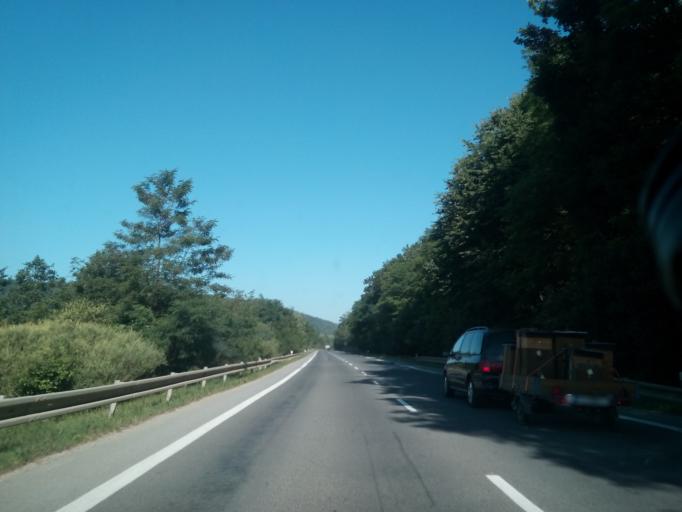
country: SK
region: Presovsky
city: Sabinov
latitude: 49.0100
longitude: 21.0608
